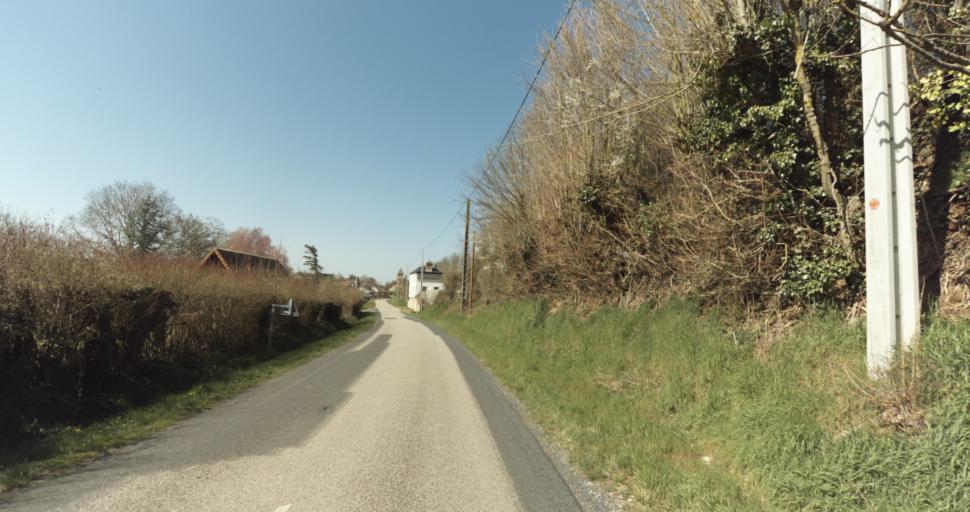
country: FR
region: Lower Normandy
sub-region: Departement du Calvados
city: Saint-Pierre-sur-Dives
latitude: 49.0162
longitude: -0.0224
